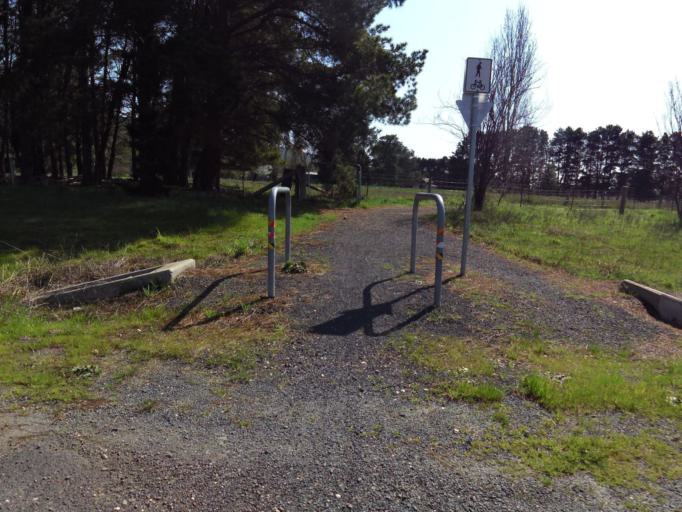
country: AU
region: Victoria
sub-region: Murrindindi
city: Alexandra
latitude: -37.1494
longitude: 145.5859
